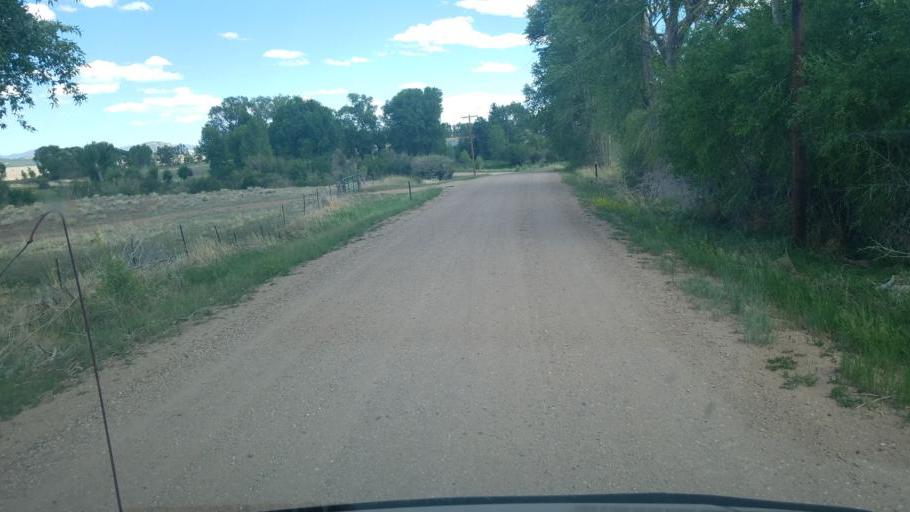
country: US
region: Colorado
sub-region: Custer County
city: Westcliffe
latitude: 38.2411
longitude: -105.6037
